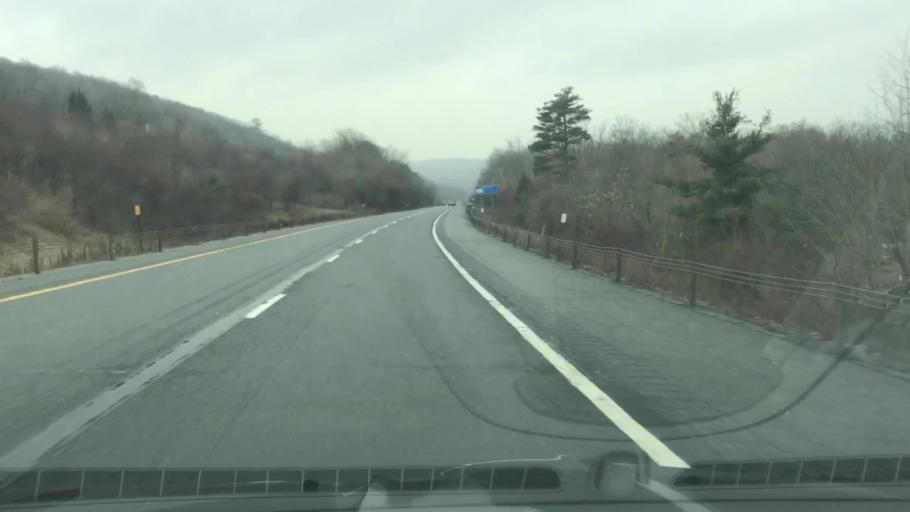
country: US
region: New York
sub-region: Orange County
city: Port Jervis
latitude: 41.3587
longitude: -74.6644
